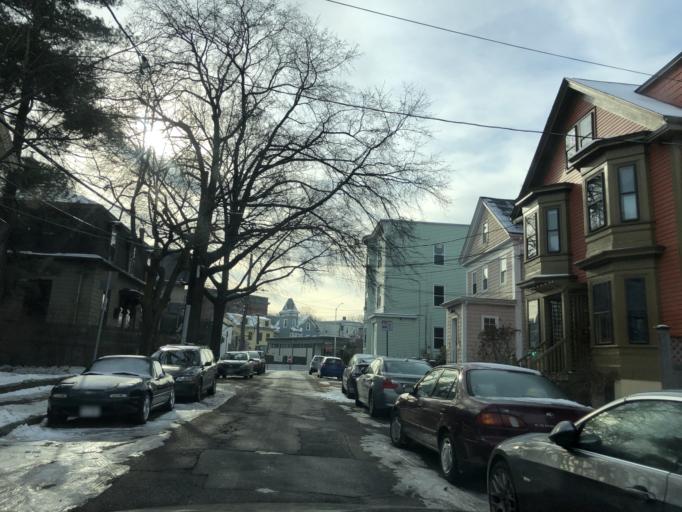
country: US
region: Massachusetts
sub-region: Middlesex County
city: Cambridge
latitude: 42.3645
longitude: -71.1089
